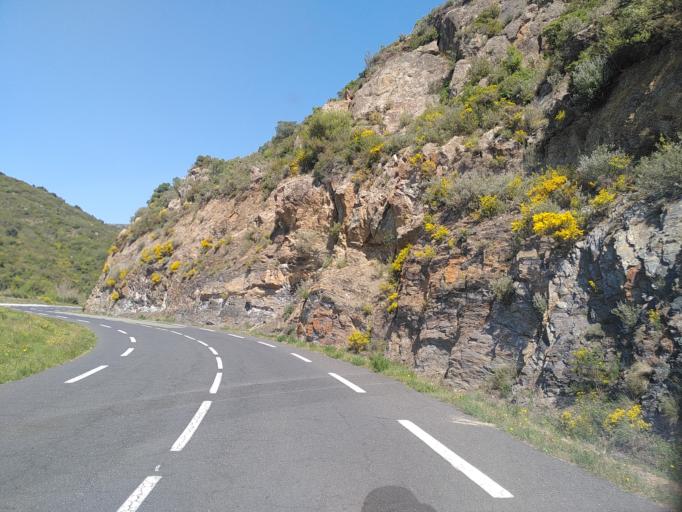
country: FR
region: Languedoc-Roussillon
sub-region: Departement de l'Aude
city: Portel-des-Corbieres
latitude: 42.9862
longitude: 2.7890
